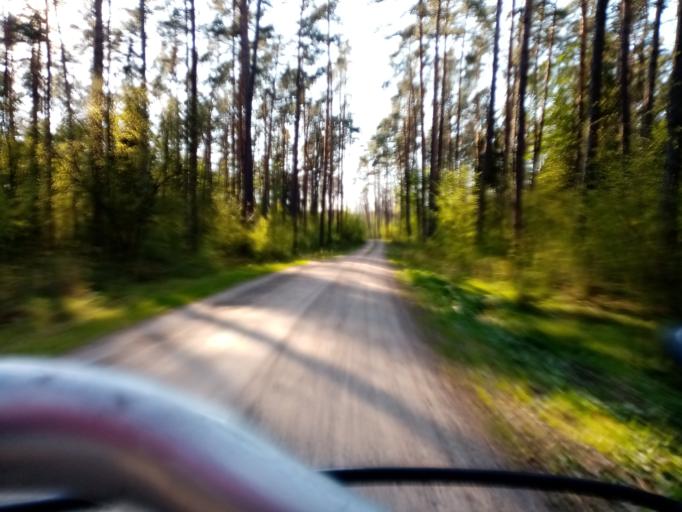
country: PL
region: Kujawsko-Pomorskie
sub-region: Powiat brodnicki
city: Gorzno
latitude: 53.1720
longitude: 19.6619
